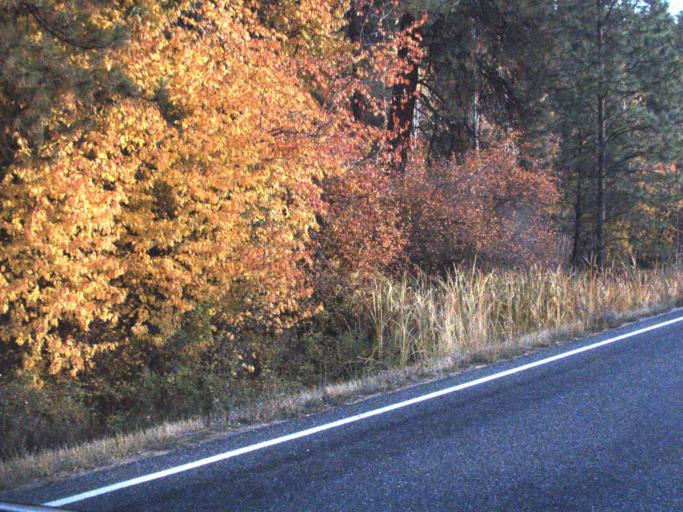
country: US
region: Washington
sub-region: Stevens County
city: Kettle Falls
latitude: 48.6946
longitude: -118.0129
